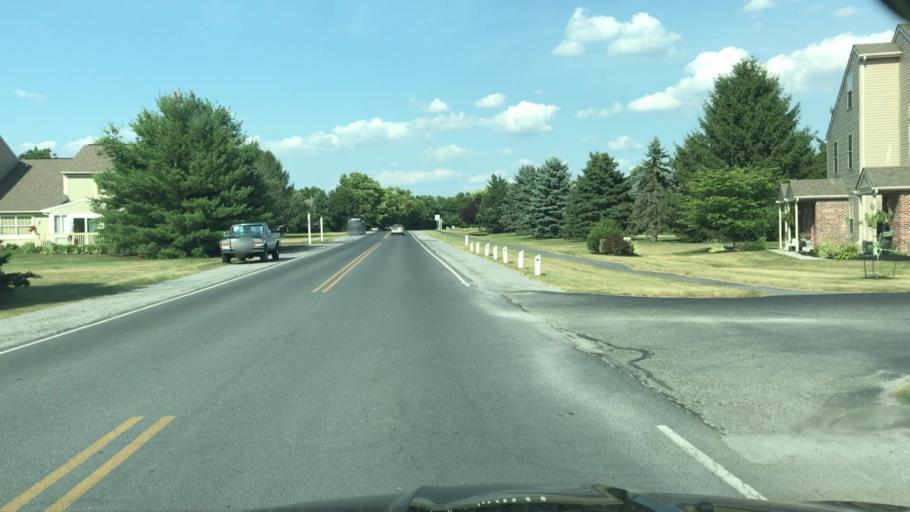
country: US
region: Pennsylvania
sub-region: Cumberland County
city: Boiling Springs
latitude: 40.1806
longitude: -77.1531
